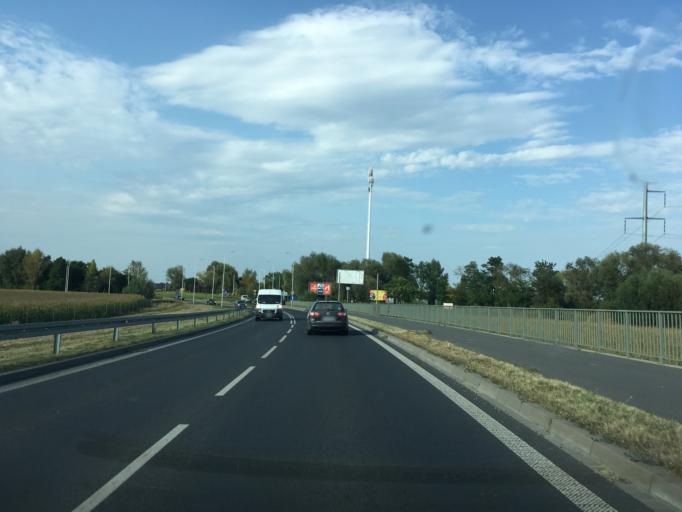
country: PL
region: Lower Silesian Voivodeship
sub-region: Powiat wroclawski
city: Kamieniec Wroclawski
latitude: 51.0846
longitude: 17.1662
